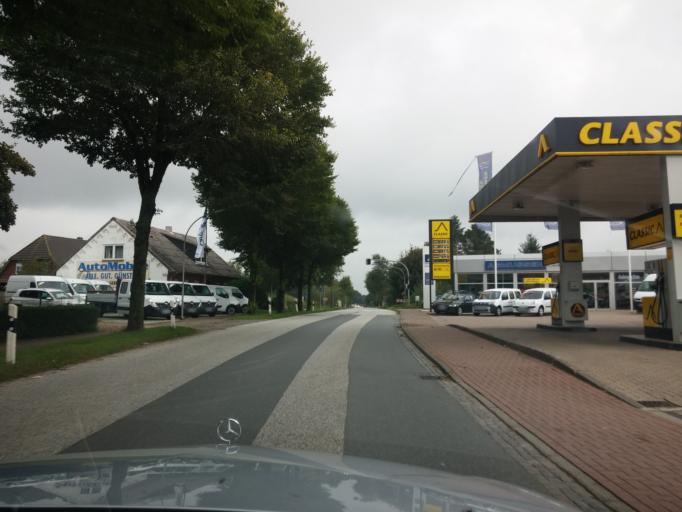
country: DE
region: Schleswig-Holstein
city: Wester-Ohrstedt
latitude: 54.5085
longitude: 9.1922
